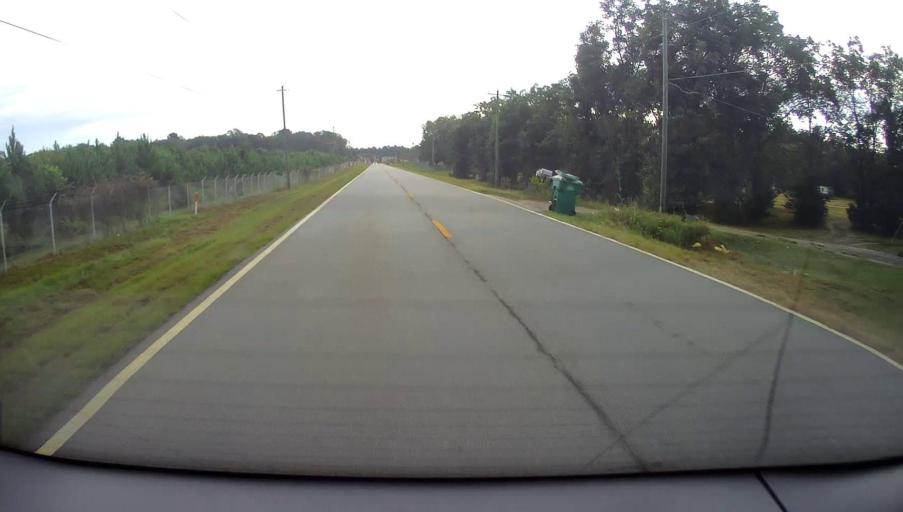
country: US
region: Georgia
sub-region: Houston County
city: Centerville
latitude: 32.6509
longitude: -83.7131
